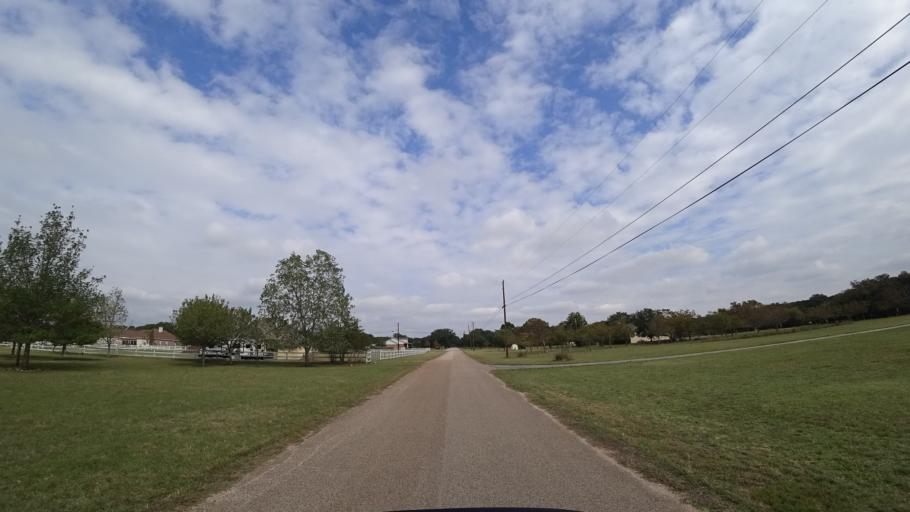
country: US
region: Texas
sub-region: Travis County
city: Shady Hollow
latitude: 30.2086
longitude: -97.8983
